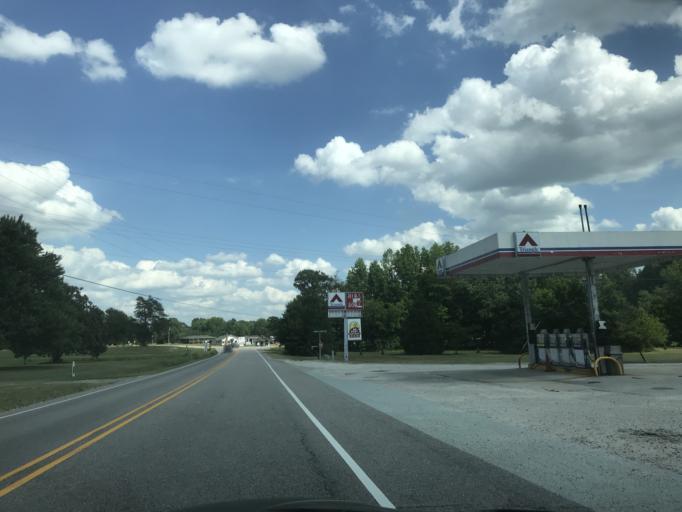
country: US
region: North Carolina
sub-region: Wake County
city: Rolesville
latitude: 35.9693
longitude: -78.3367
